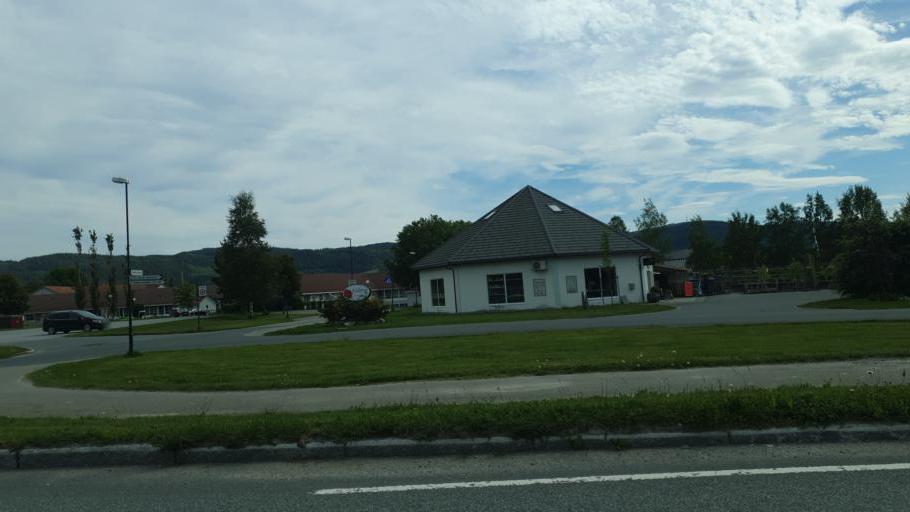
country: NO
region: Sor-Trondelag
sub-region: Rissa
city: Rissa
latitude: 63.5828
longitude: 9.9515
